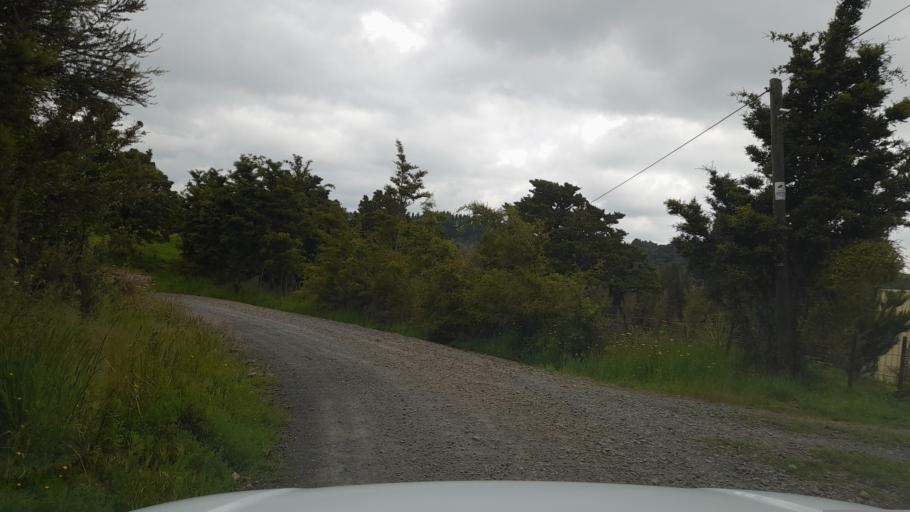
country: NZ
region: Northland
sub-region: Far North District
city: Waimate North
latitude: -35.3969
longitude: 173.7847
